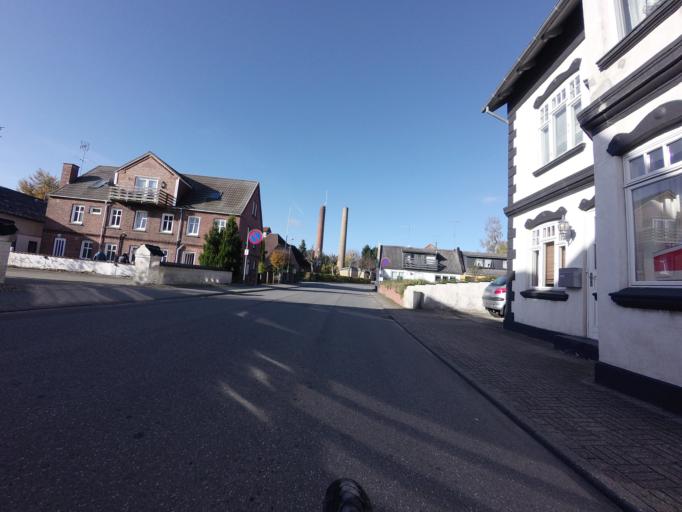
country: DK
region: Central Jutland
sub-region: Syddjurs Kommune
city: Ryomgard
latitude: 56.4092
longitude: 10.5658
